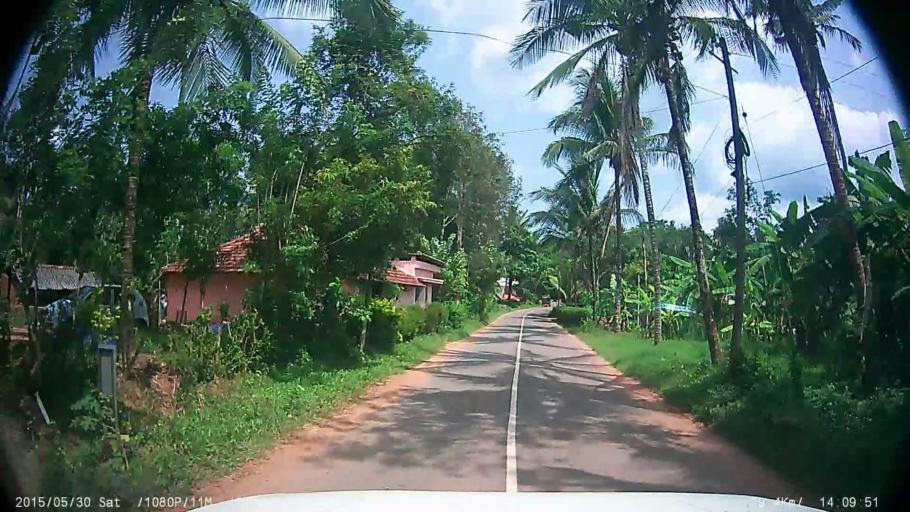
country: IN
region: Kerala
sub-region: Wayanad
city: Panamaram
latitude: 11.8033
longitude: 76.0515
